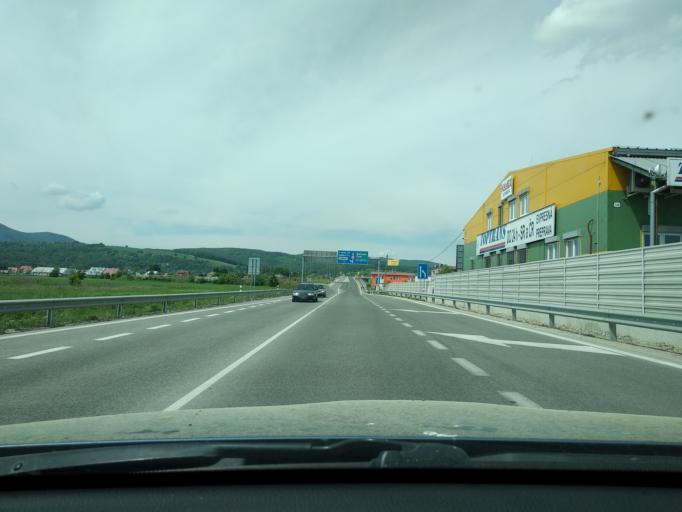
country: SK
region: Trenciansky
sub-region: Okres Trencin
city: Trencin
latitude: 48.8899
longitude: 18.0072
